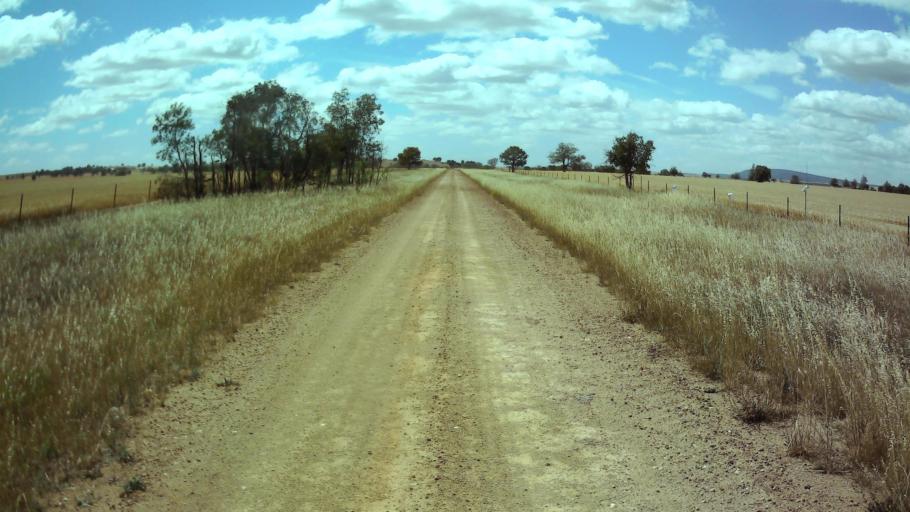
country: AU
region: New South Wales
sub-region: Weddin
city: Grenfell
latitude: -33.9893
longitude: 148.3226
